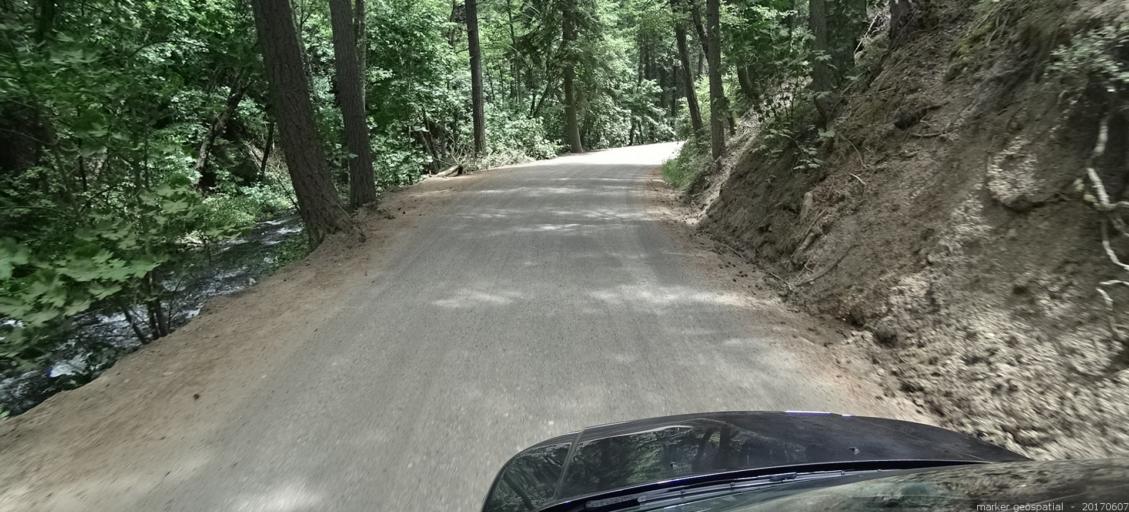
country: US
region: California
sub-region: Siskiyou County
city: Mount Shasta
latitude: 41.2918
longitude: -122.3251
